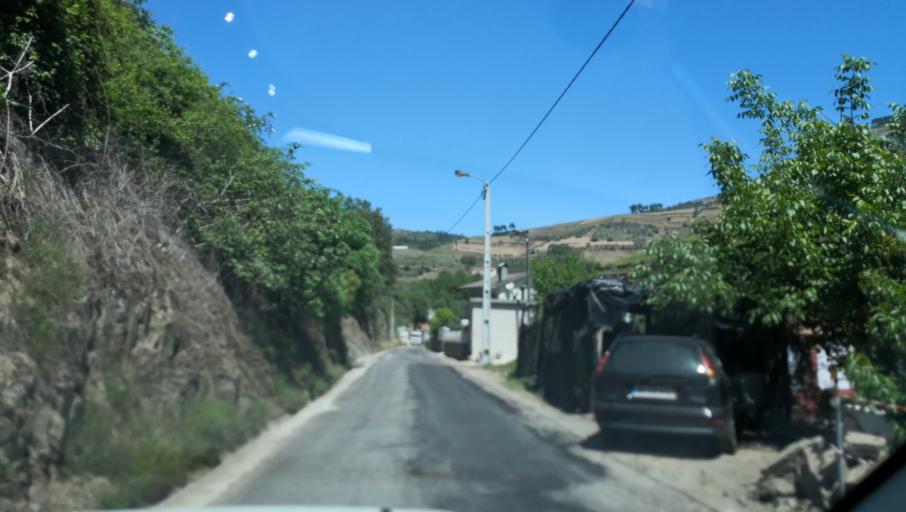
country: PT
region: Vila Real
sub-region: Santa Marta de Penaguiao
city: Santa Marta de Penaguiao
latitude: 41.2206
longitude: -7.7230
